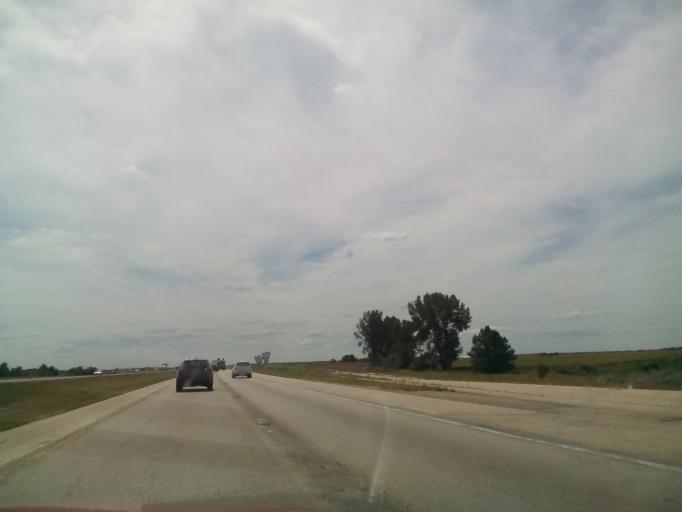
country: US
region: Illinois
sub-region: Ogle County
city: Hillcrest
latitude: 41.9712
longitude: -89.0217
